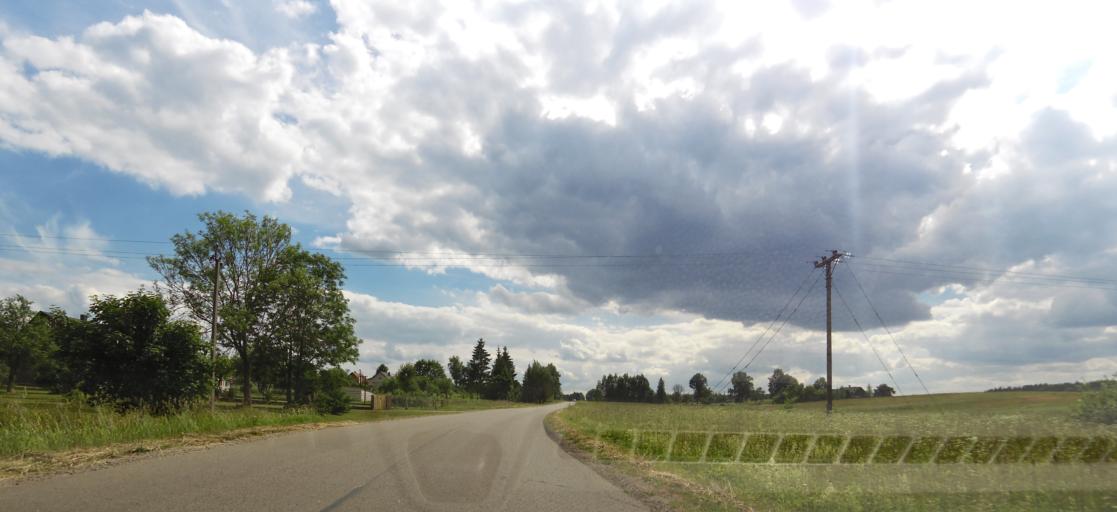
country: LT
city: Skaidiskes
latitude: 54.5360
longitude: 25.6448
